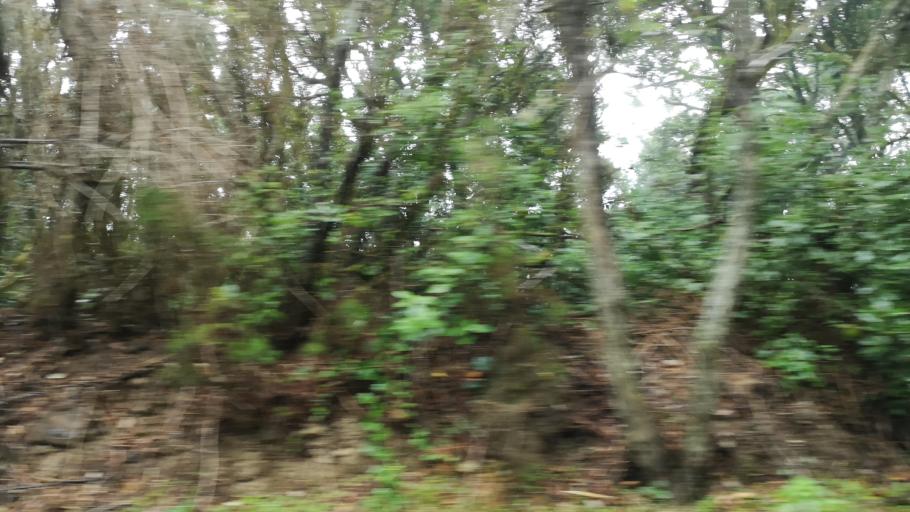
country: ES
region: Canary Islands
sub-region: Provincia de Santa Cruz de Tenerife
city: Hermigua
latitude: 28.1220
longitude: -17.2128
